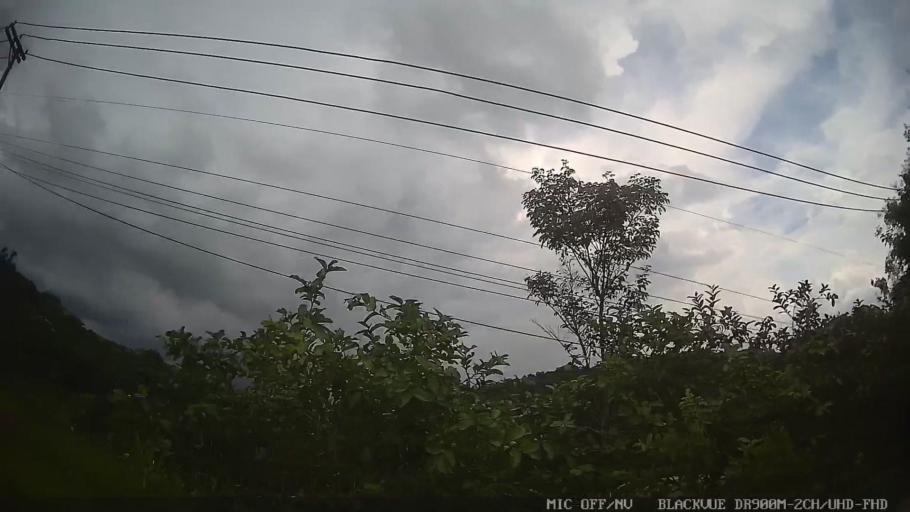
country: BR
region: Sao Paulo
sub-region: Mogi das Cruzes
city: Mogi das Cruzes
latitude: -23.4487
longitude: -46.2263
